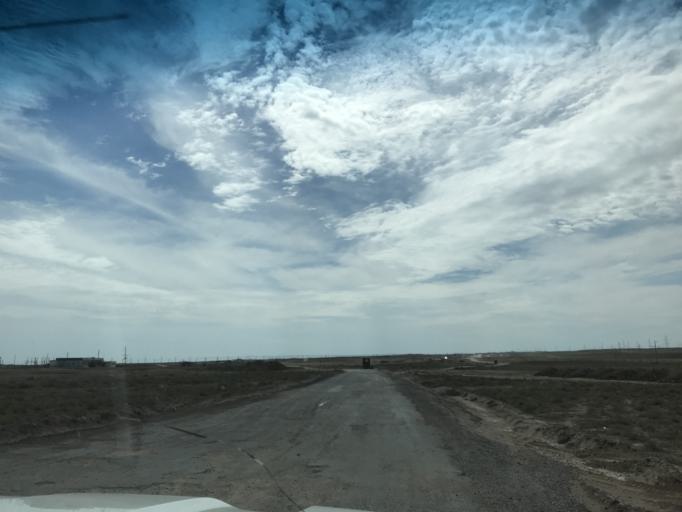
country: KZ
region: Almaty Oblysy
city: Ulken
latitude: 45.2475
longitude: 73.8156
